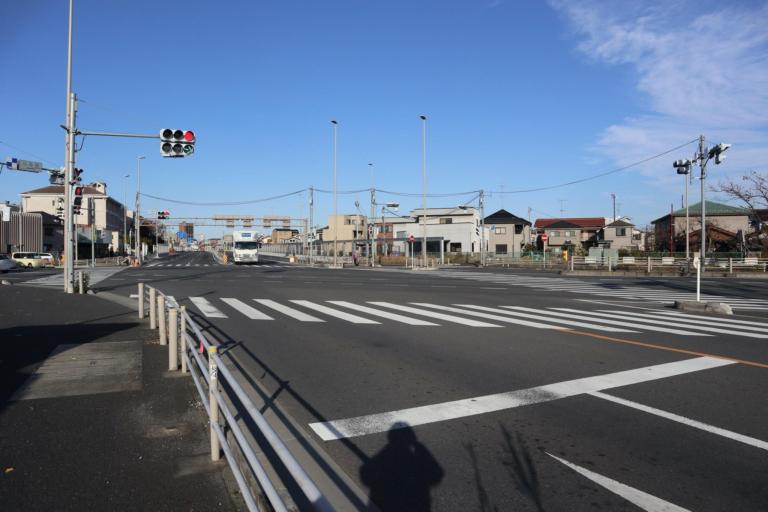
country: JP
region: Tokyo
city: Fussa
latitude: 35.7138
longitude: 139.3382
